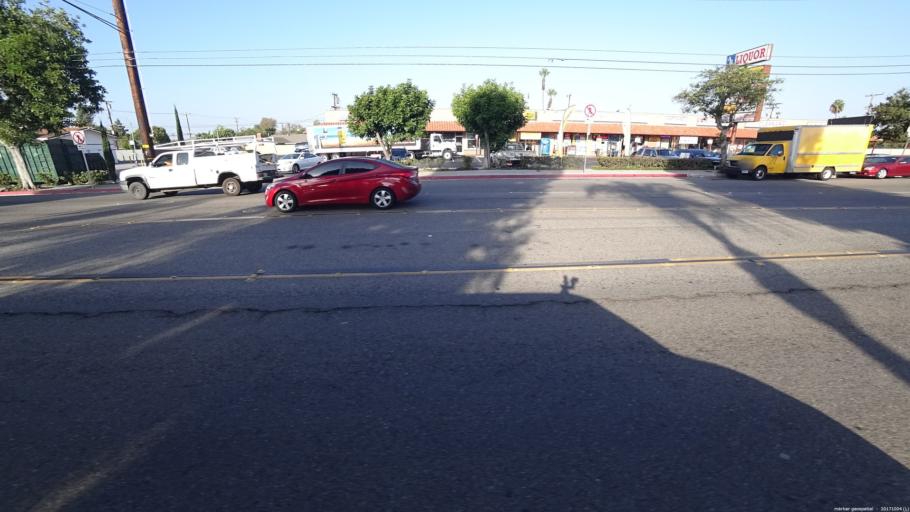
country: US
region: California
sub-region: Orange County
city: Garden Grove
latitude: 33.7824
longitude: -117.9061
